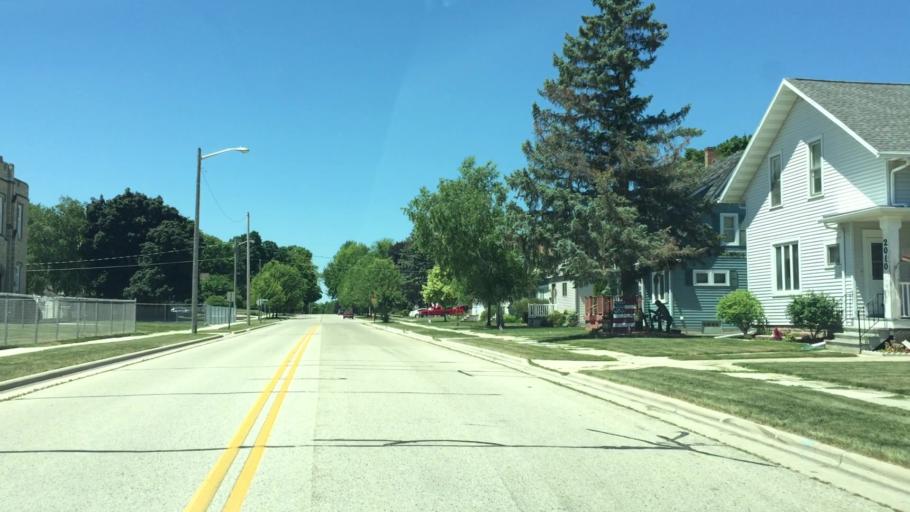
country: US
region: Wisconsin
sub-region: Calumet County
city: New Holstein
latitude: 43.9487
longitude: -88.0926
